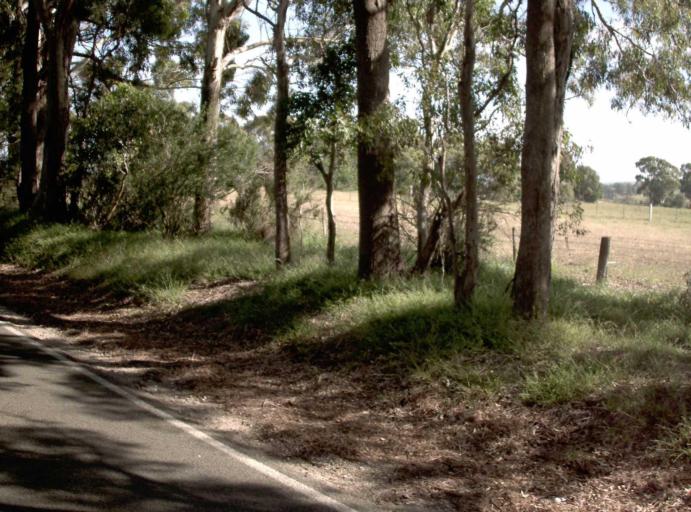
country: AU
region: Victoria
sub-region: East Gippsland
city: Lakes Entrance
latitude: -37.8130
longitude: 147.8475
